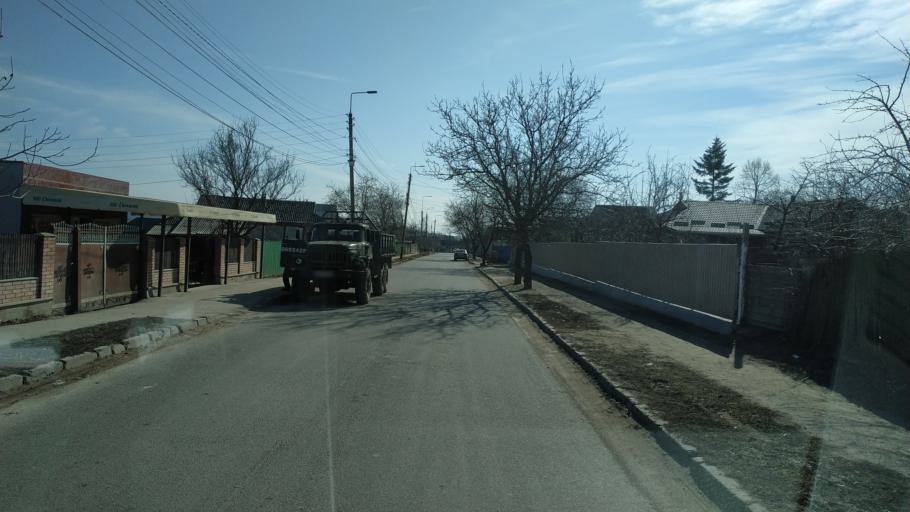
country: MD
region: Nisporeni
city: Nisporeni
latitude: 47.0753
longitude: 28.1695
